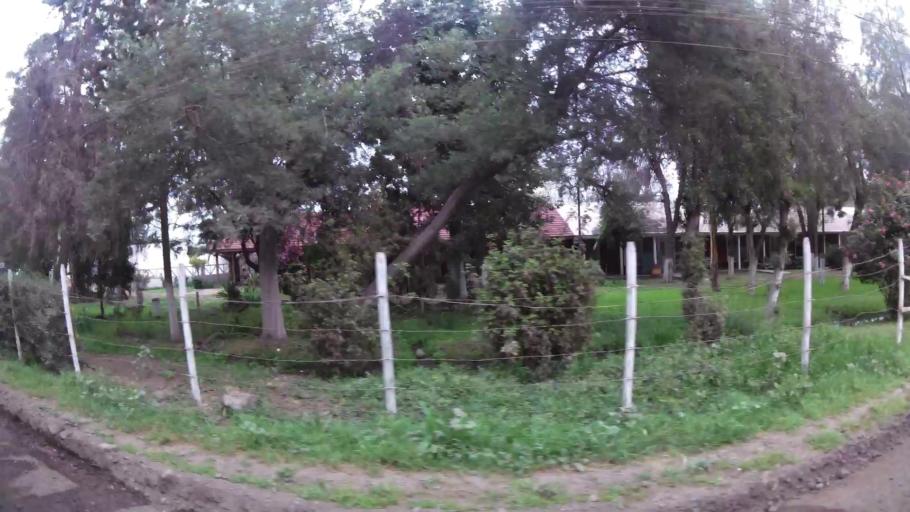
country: CL
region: Santiago Metropolitan
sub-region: Provincia de Chacabuco
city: Chicureo Abajo
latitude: -33.2110
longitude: -70.6600
